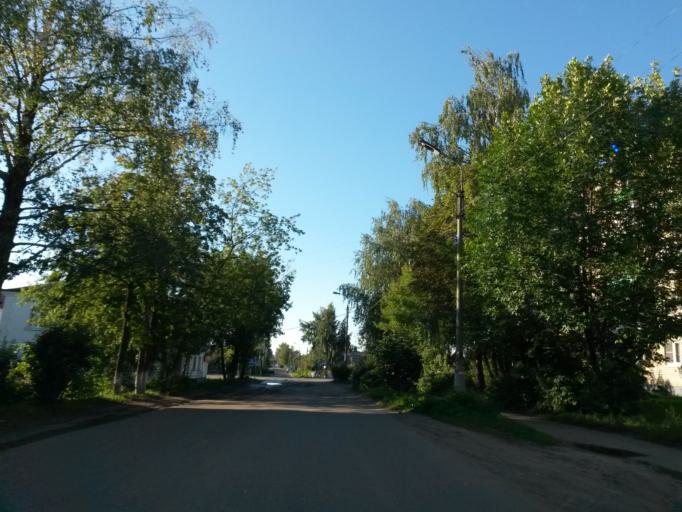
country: RU
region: Jaroslavl
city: Gavrilov-Yam
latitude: 57.3051
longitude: 39.8614
